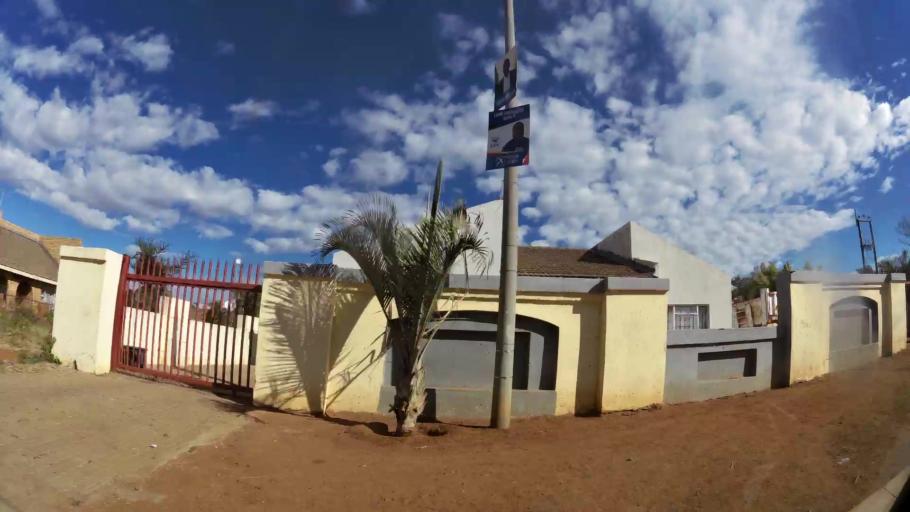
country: ZA
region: Limpopo
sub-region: Waterberg District Municipality
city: Warmbaths
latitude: -24.8786
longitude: 28.2731
